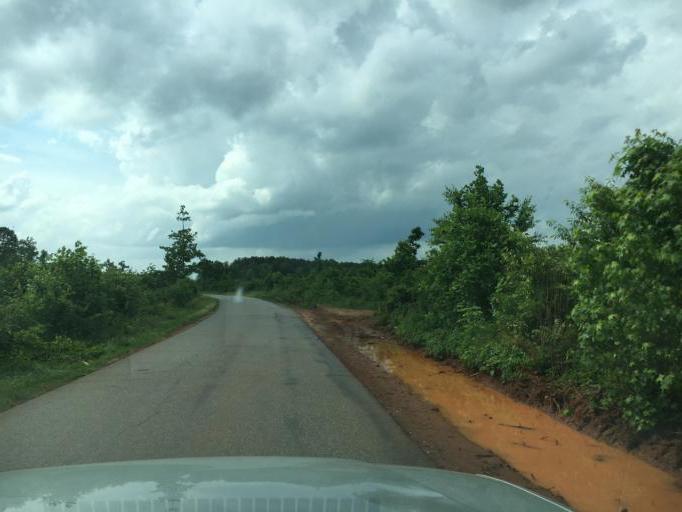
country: US
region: South Carolina
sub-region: Spartanburg County
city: Fairforest
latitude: 34.9216
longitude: -82.0484
